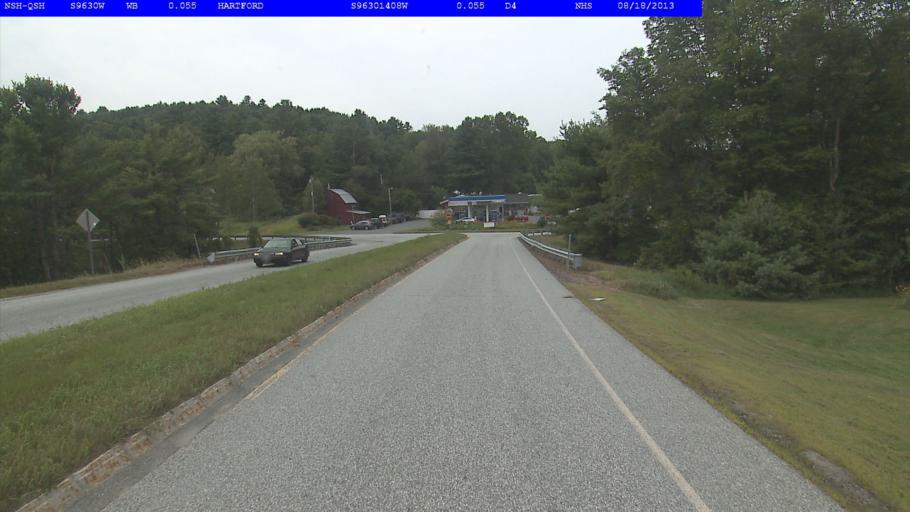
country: US
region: Vermont
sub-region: Windsor County
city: White River Junction
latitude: 43.6624
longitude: -72.3866
